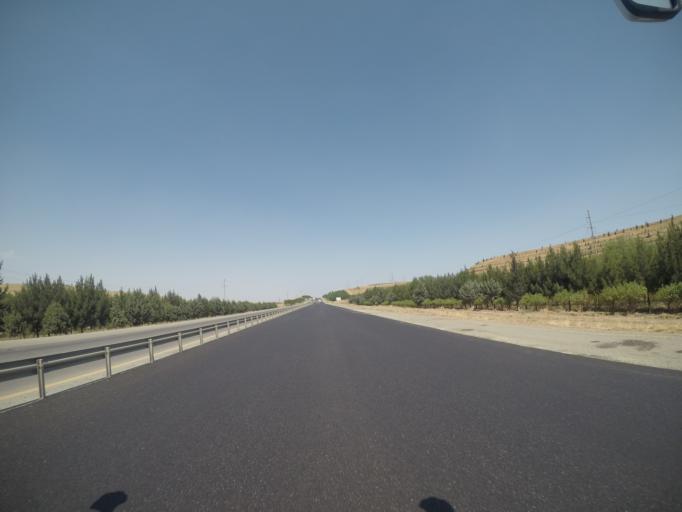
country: AZ
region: Haciqabul
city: Haciqabul
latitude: 40.0434
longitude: 48.9677
